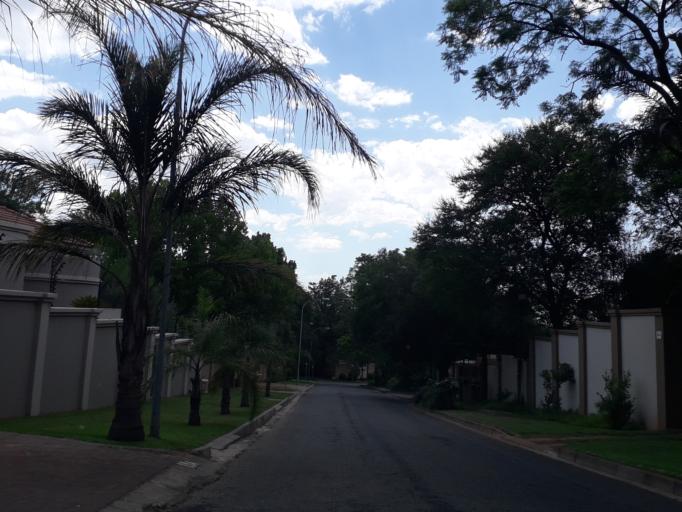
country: ZA
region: Gauteng
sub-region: City of Johannesburg Metropolitan Municipality
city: Roodepoort
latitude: -26.1387
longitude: 27.9651
